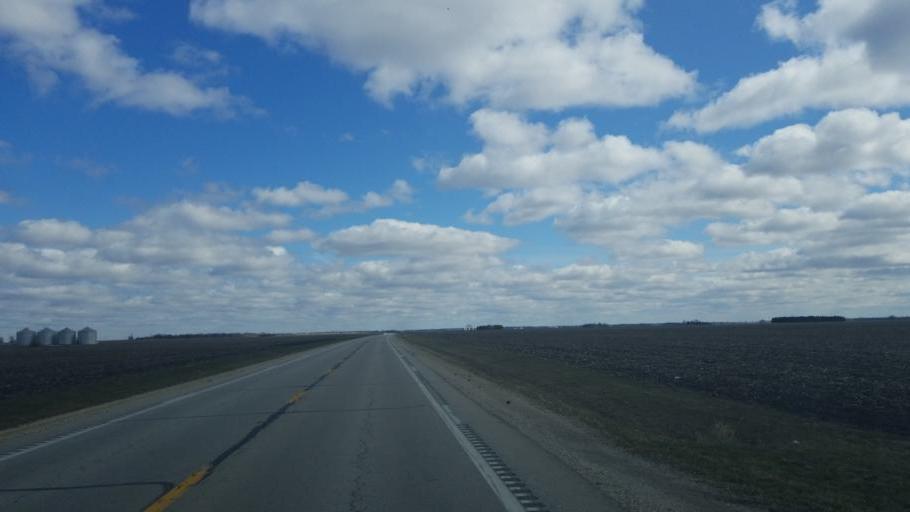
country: US
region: Illinois
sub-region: Douglas County
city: Villa Grove
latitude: 39.7919
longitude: -88.1256
